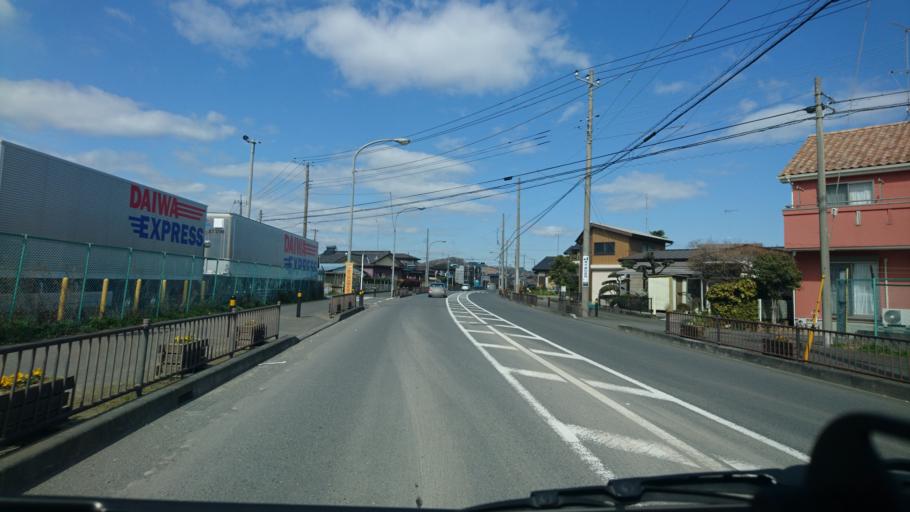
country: JP
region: Kanagawa
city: Zama
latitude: 35.5284
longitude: 139.3356
